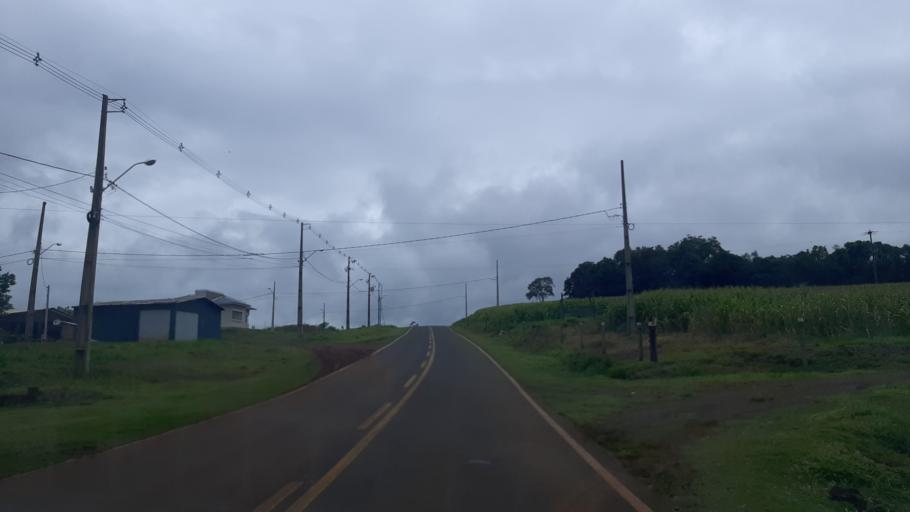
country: BR
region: Parana
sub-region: Ampere
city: Ampere
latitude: -25.9330
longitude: -53.4651
